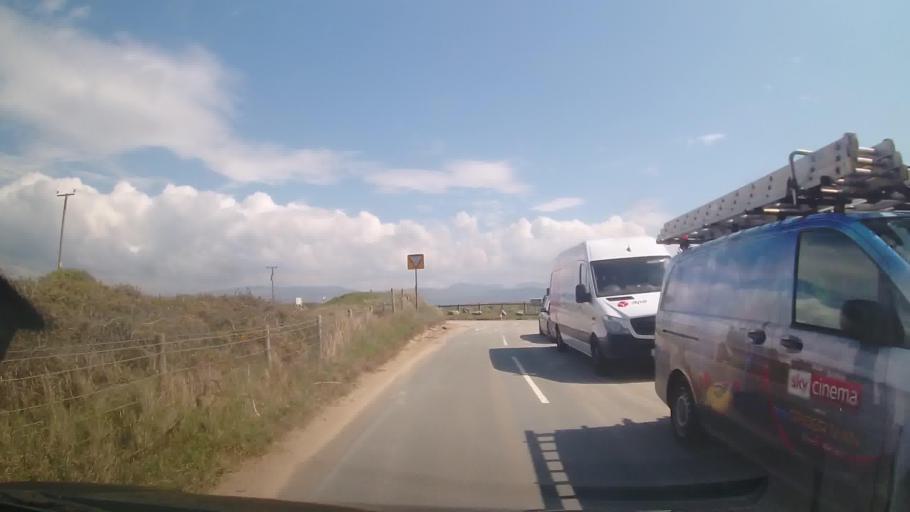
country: GB
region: Wales
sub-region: Gwynedd
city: Criccieth
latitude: 52.9133
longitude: -4.1879
